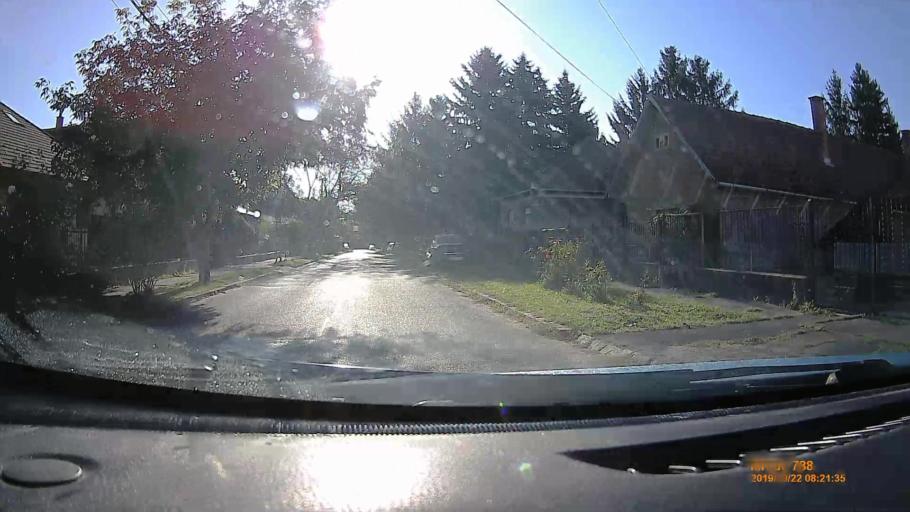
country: HU
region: Borsod-Abauj-Zemplen
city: Sajobabony
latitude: 48.0978
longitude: 20.6971
